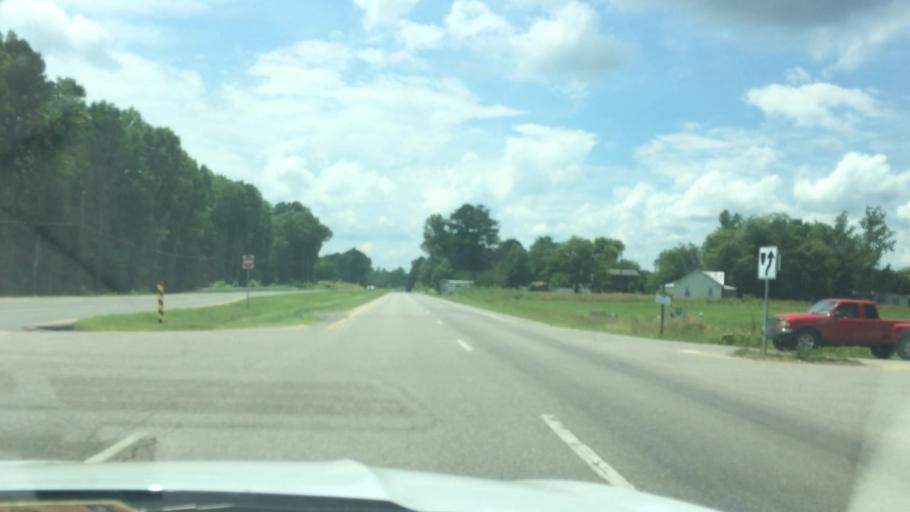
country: US
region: Virginia
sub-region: King William County
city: West Point
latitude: 37.5465
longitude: -76.7162
